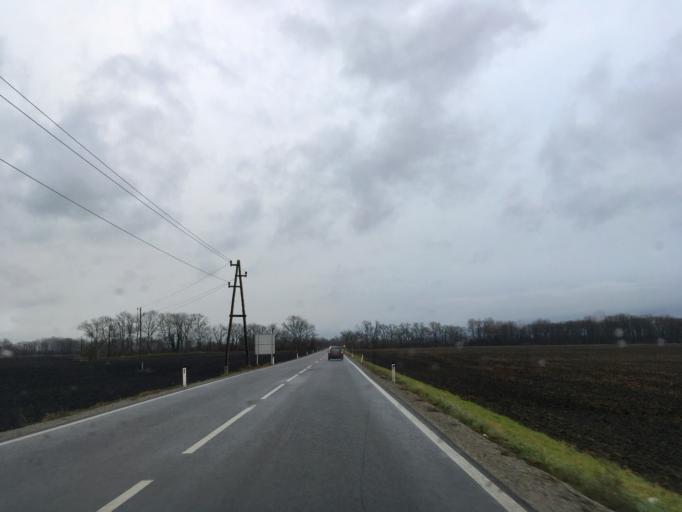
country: AT
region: Lower Austria
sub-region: Politischer Bezirk Wien-Umgebung
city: Ebergassing
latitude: 48.0425
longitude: 16.5259
